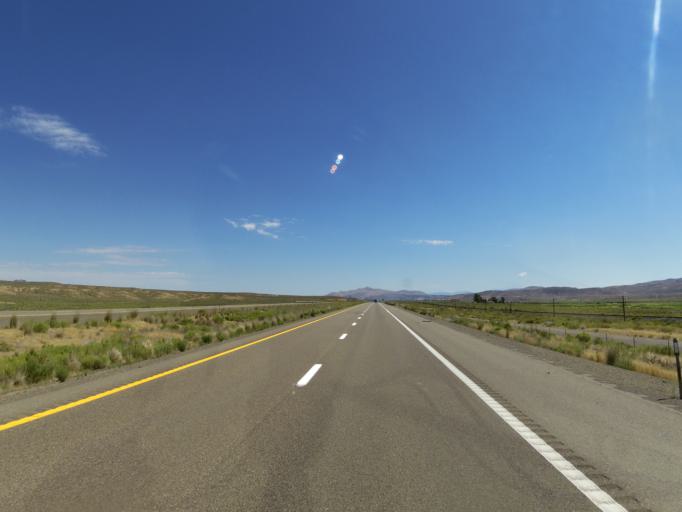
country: US
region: Nevada
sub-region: Elko County
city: Elko
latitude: 40.7851
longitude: -115.8683
